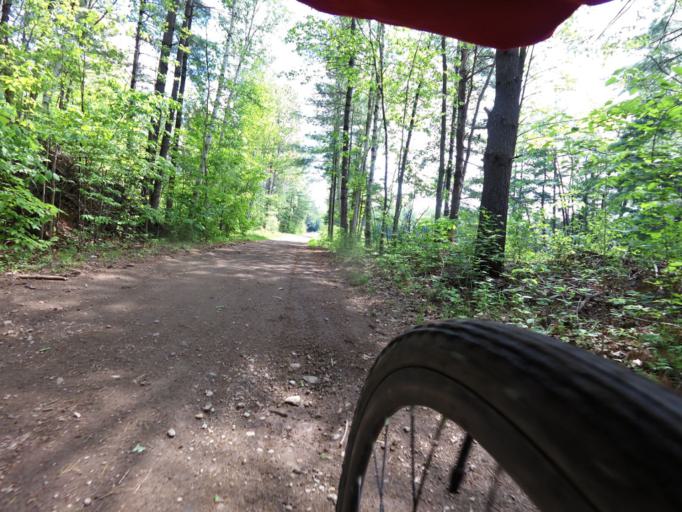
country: CA
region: Ontario
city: Renfrew
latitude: 45.2177
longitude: -76.6927
